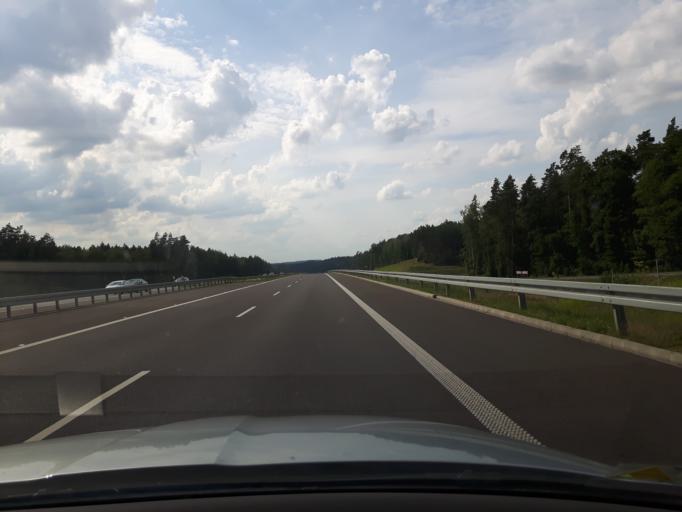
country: PL
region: Warmian-Masurian Voivodeship
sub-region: Powiat ostrodzki
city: Gierzwald
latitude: 53.5859
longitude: 20.1569
